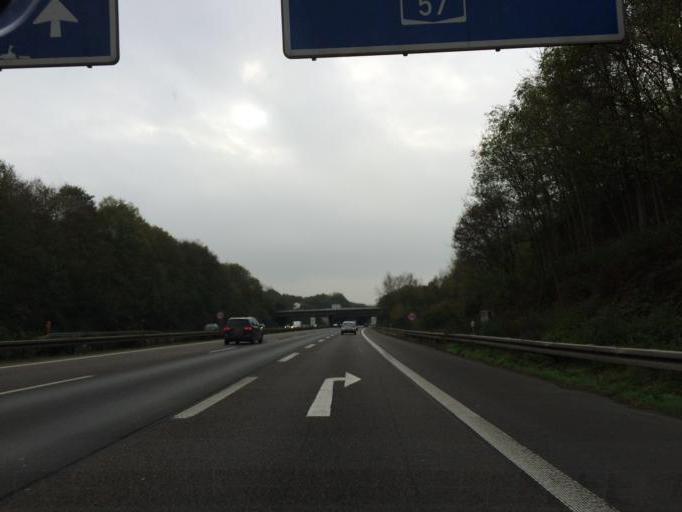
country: DE
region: North Rhine-Westphalia
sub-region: Regierungsbezirk Koln
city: Bilderstoeckchen
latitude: 51.0028
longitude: 6.9033
